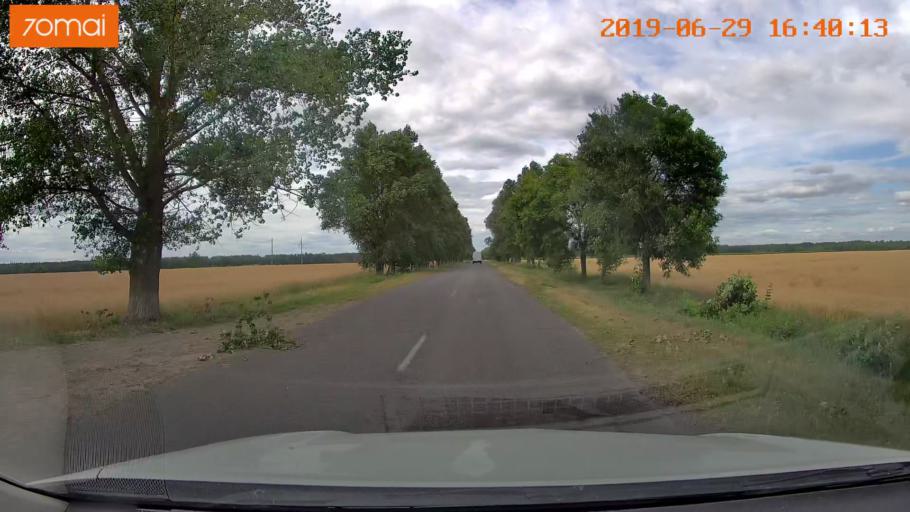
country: BY
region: Brest
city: Luninyets
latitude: 52.2528
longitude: 27.0170
